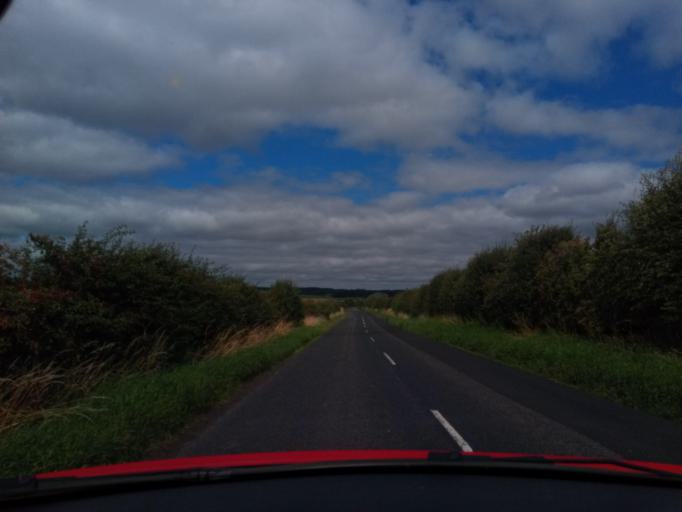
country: GB
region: Scotland
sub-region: The Scottish Borders
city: Kelso
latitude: 55.5386
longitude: -2.3673
